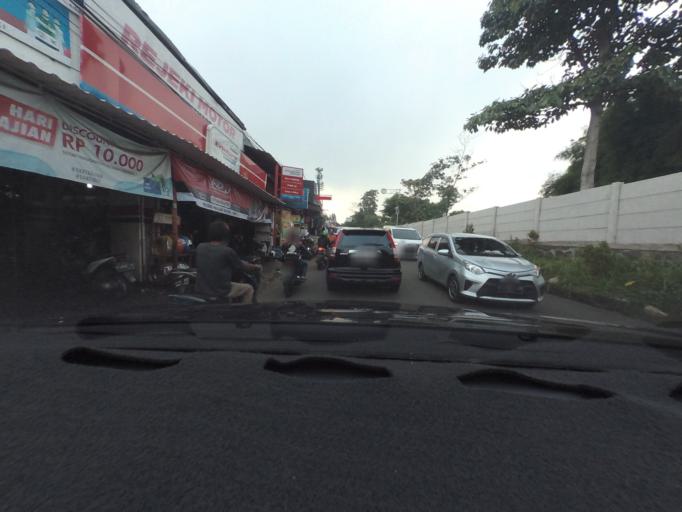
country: ID
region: West Java
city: Bogor
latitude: -6.6007
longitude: 106.8135
